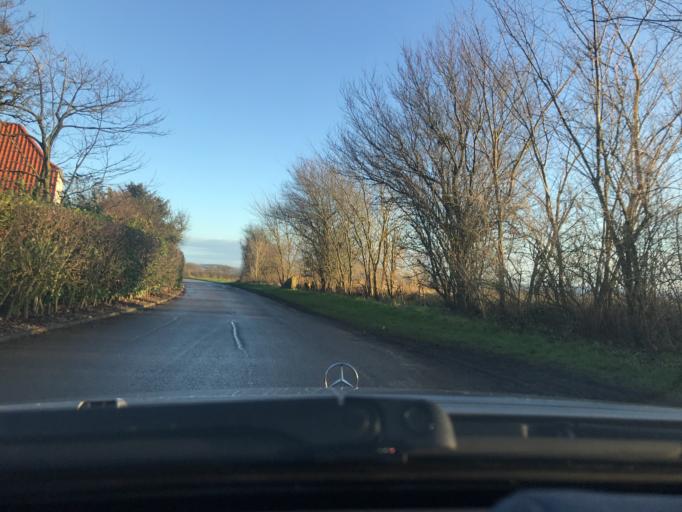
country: DK
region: South Denmark
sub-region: Sonderborg Kommune
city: Dybbol
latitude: 54.9022
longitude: 9.7621
